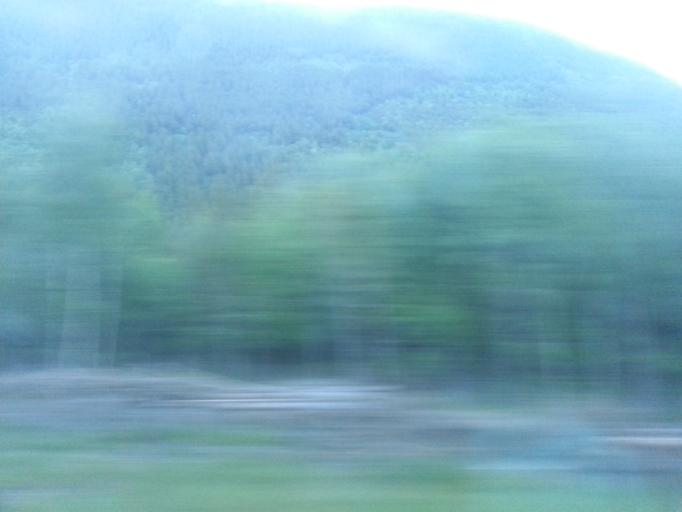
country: NO
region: Oppland
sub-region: Dovre
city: Dovre
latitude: 61.9433
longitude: 9.3010
